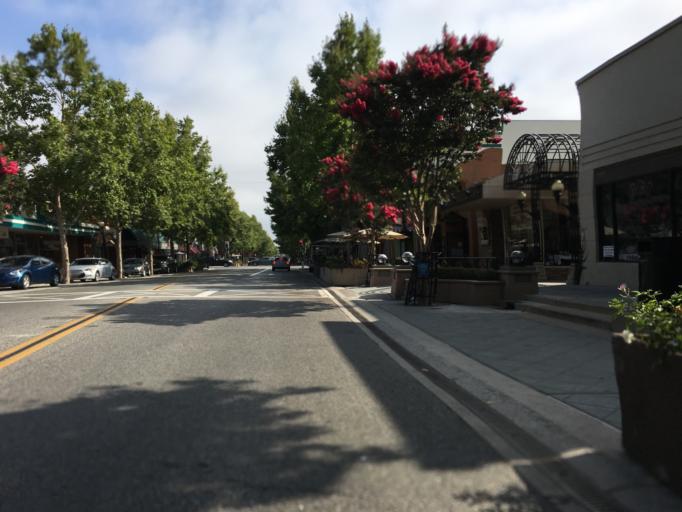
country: US
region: California
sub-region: Santa Clara County
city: Mountain View
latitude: 37.3918
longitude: -122.0801
